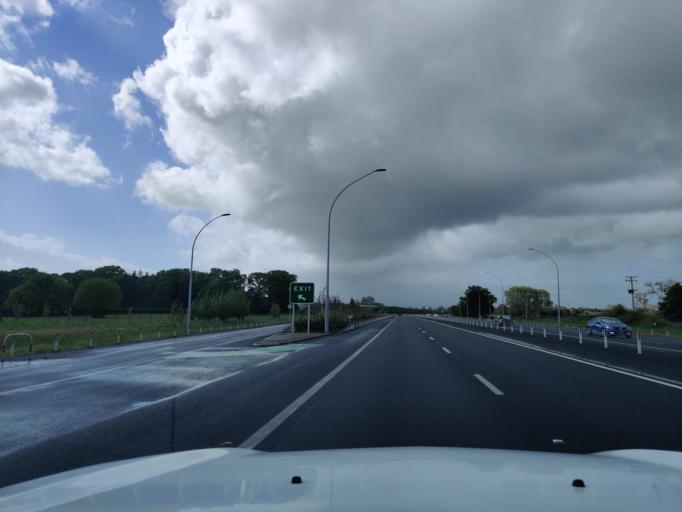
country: NZ
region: Waikato
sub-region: Waipa District
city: Cambridge
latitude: -37.8630
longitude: 175.4008
